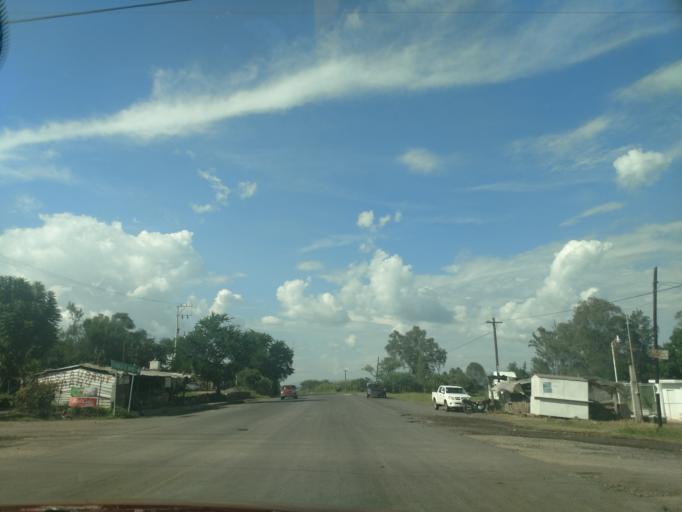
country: MX
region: Jalisco
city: Antonio Escobedo
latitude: 20.8483
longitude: -104.0290
